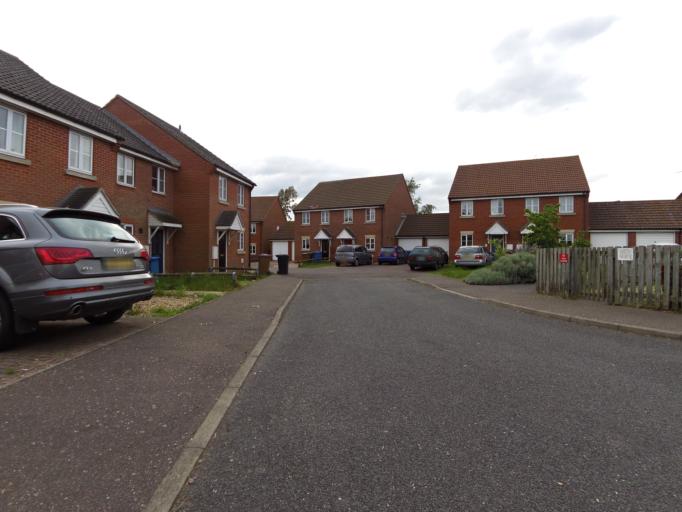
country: GB
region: England
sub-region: Suffolk
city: Ipswich
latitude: 52.0361
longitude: 1.1669
